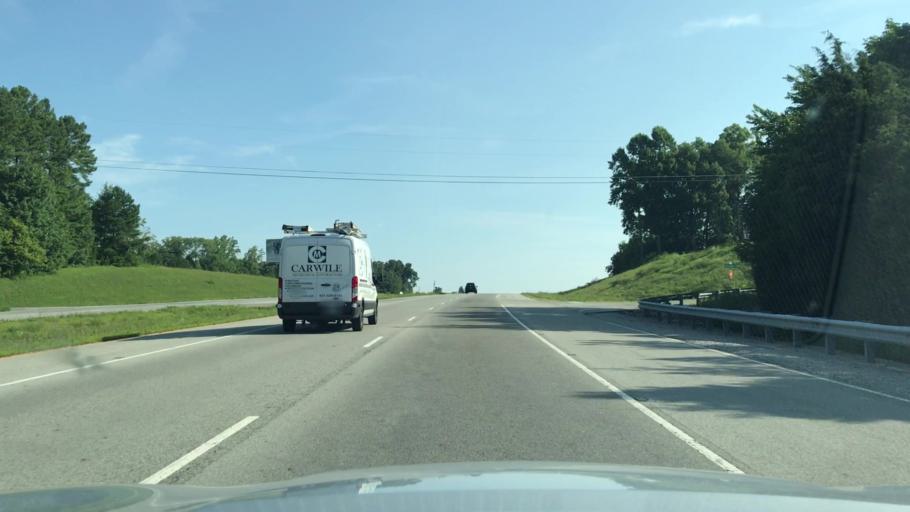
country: US
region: Tennessee
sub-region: Putnam County
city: Algood
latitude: 36.2647
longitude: -85.3912
